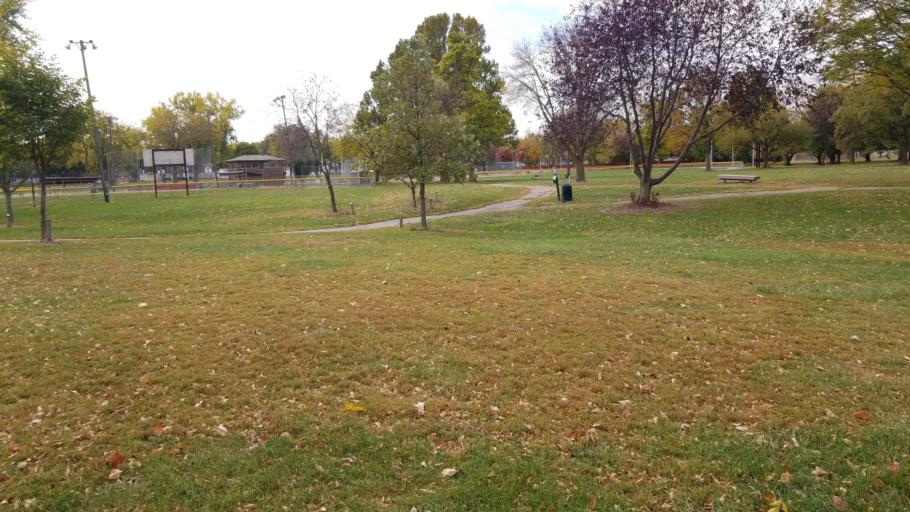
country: US
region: Nebraska
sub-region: Sarpy County
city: Papillion
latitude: 41.1533
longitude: -96.0339
